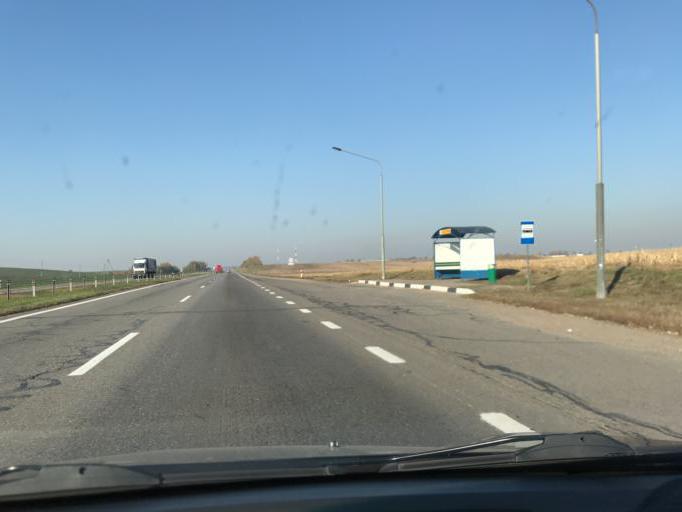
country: BY
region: Minsk
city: Luhavaya Slabada
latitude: 53.7234
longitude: 27.8604
